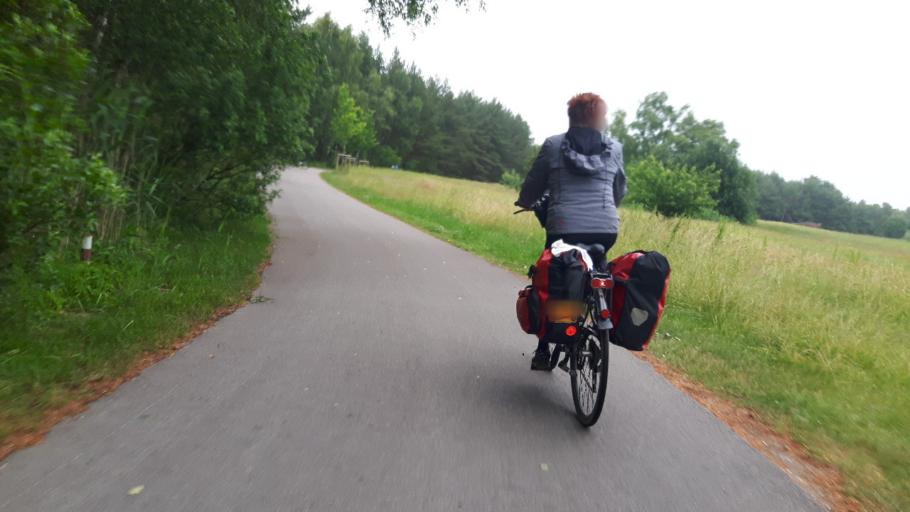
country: LT
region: Klaipedos apskritis
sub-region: Palanga
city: Sventoji
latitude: 55.9904
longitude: 21.0746
